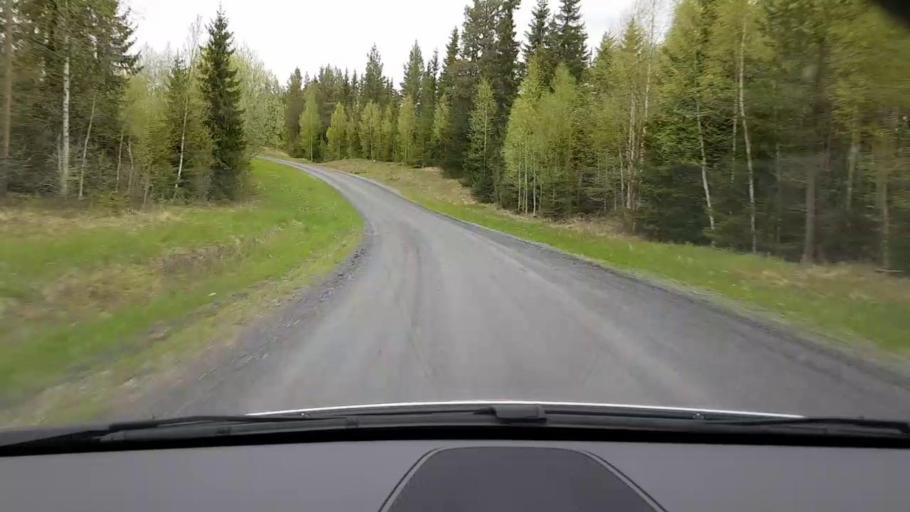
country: SE
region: Jaemtland
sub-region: Krokoms Kommun
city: Krokom
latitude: 63.2988
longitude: 14.3970
